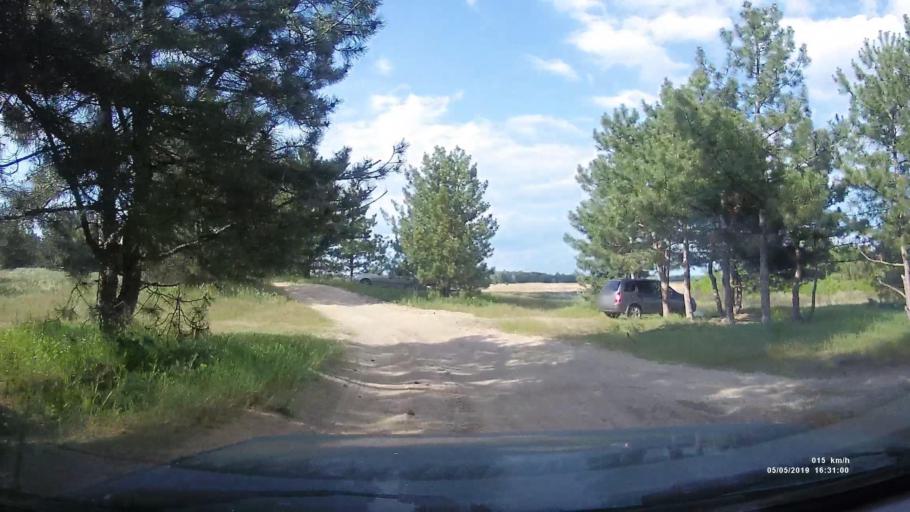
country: RU
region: Rostov
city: Ust'-Donetskiy
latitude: 47.7752
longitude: 41.0153
